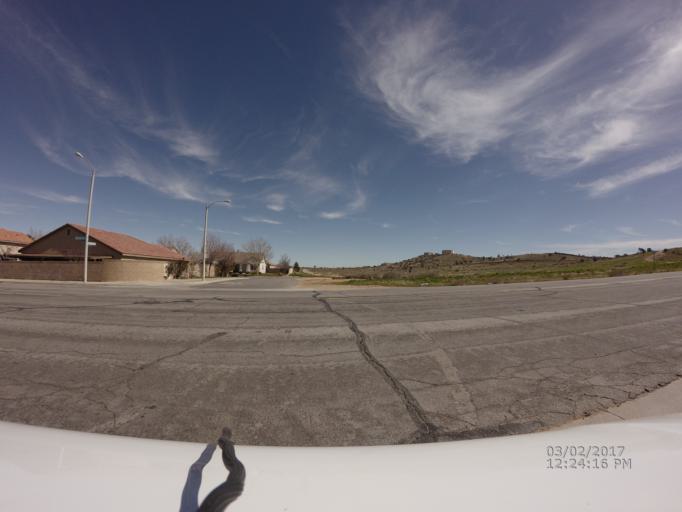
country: US
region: California
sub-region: Los Angeles County
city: Quartz Hill
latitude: 34.6493
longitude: -118.2102
